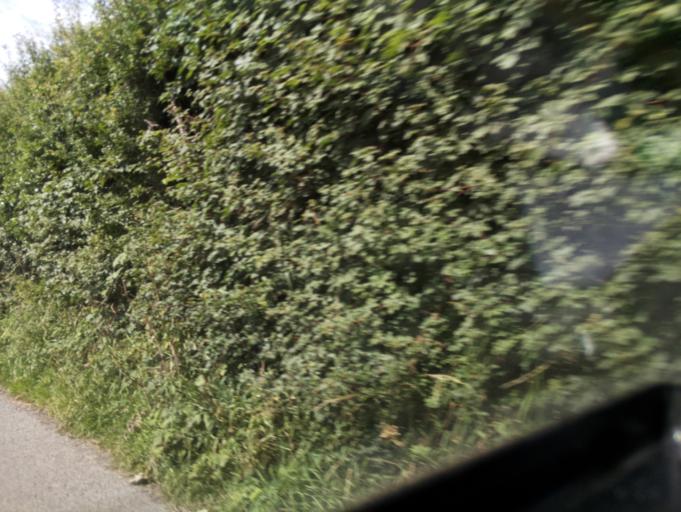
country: GB
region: England
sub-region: South Gloucestershire
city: Horton
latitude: 51.5365
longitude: -2.3615
